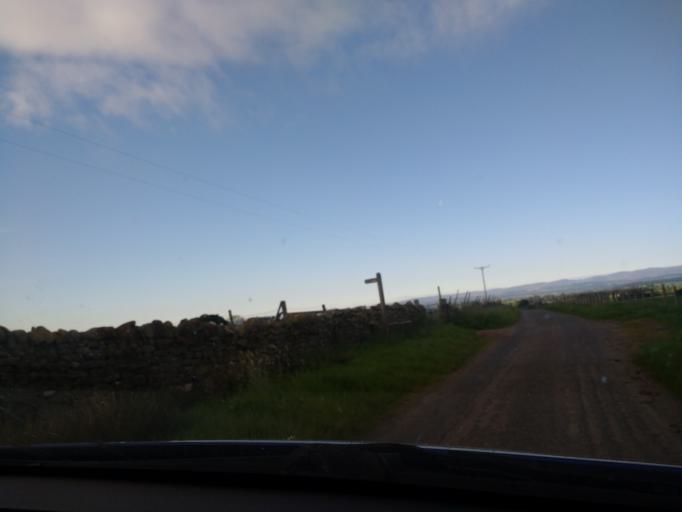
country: GB
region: England
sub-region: Cumbria
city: Appleby-in-Westmorland
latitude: 54.6832
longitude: -2.5547
